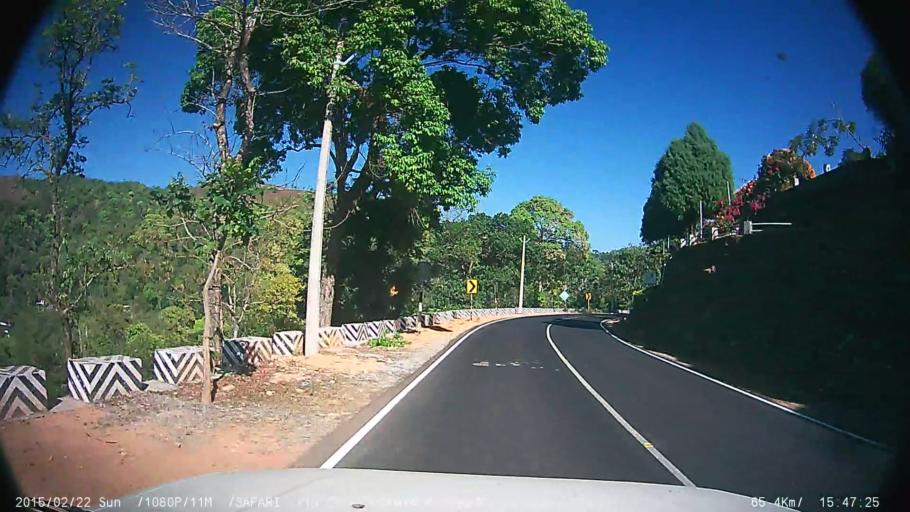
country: IN
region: Kerala
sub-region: Kottayam
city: Erattupetta
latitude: 9.5771
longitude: 76.9897
